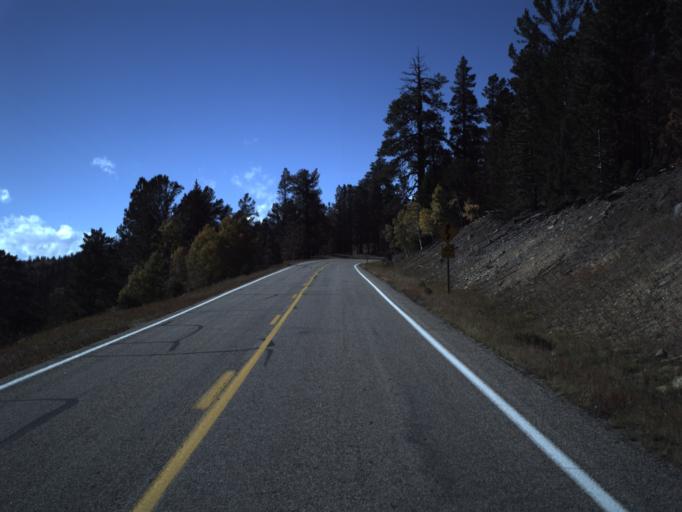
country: US
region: Utah
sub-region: Iron County
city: Parowan
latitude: 37.6522
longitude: -112.6984
